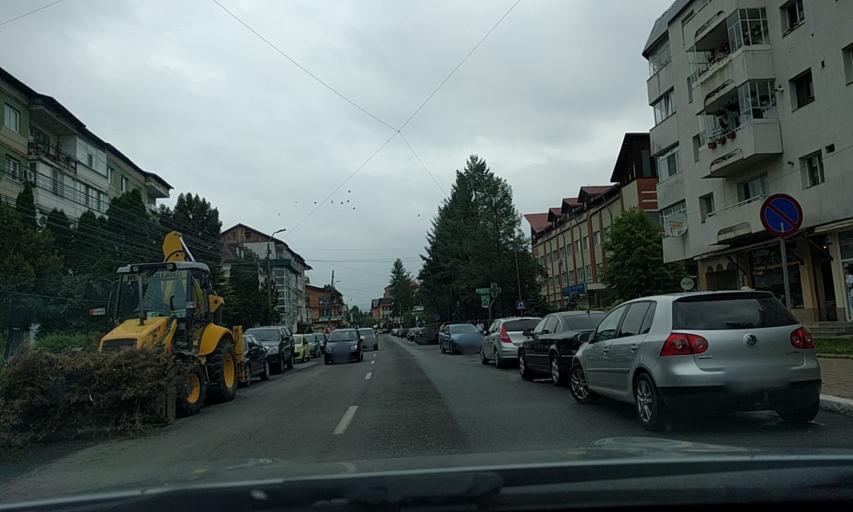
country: RO
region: Dambovita
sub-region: Oras Pucioasa
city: Pucioasa
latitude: 45.0744
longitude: 25.4350
